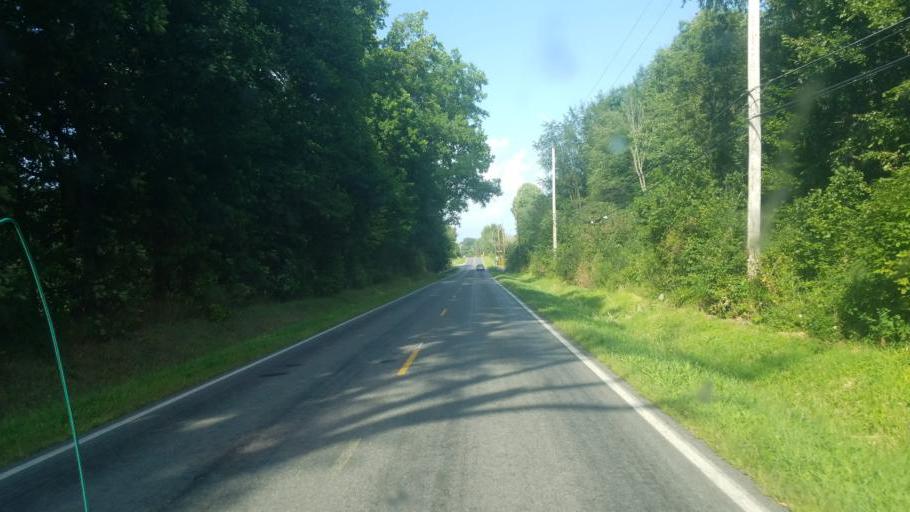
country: US
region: Ohio
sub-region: Medina County
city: Lodi
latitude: 41.0227
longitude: -82.0364
